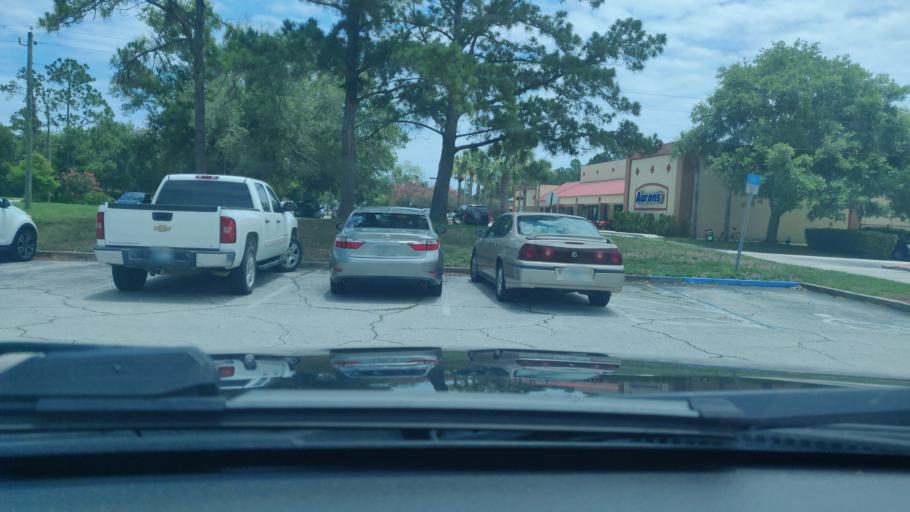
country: US
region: Florida
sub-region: Flagler County
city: Palm Coast
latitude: 29.5521
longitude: -81.2521
